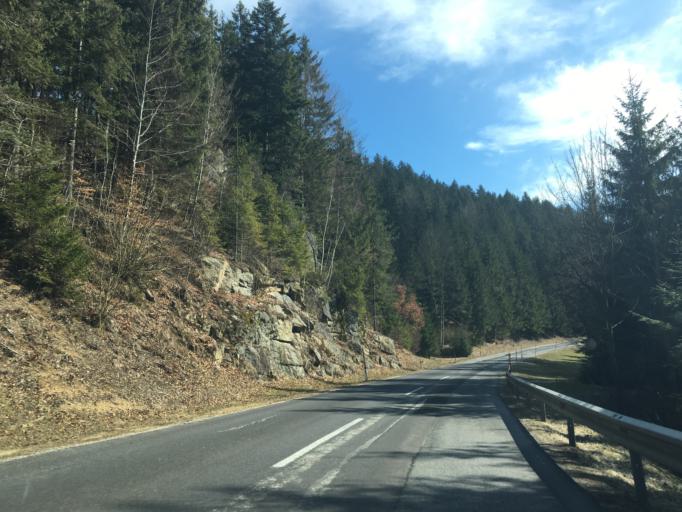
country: AT
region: Upper Austria
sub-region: Politischer Bezirk Perg
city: Sankt Georgen am Walde
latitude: 48.4007
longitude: 14.8588
